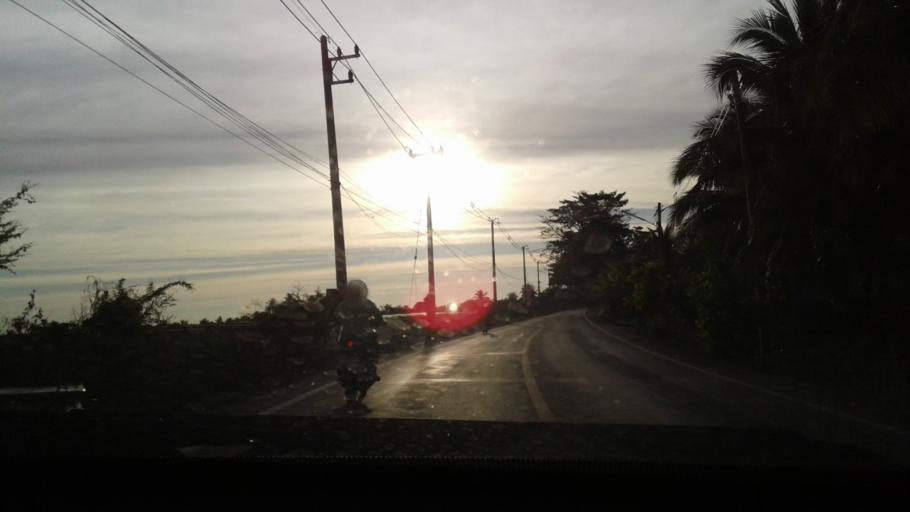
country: TH
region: Nonthaburi
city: Sai Noi
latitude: 13.9012
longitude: 100.2488
